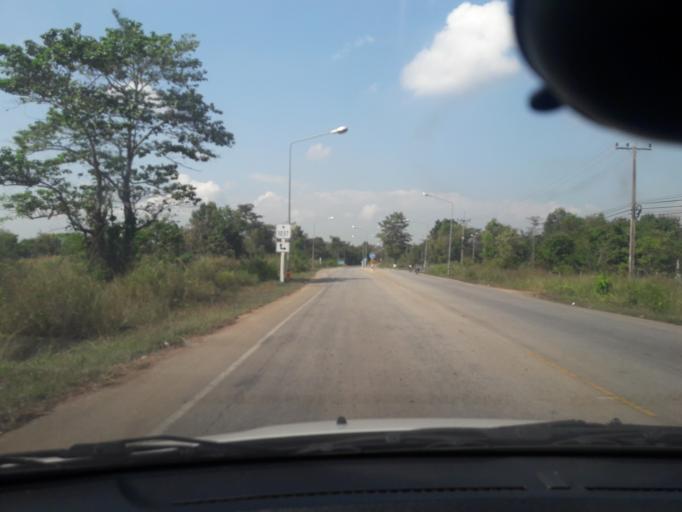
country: TH
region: Lampang
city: Mae Tha
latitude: 18.1980
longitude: 99.5093
